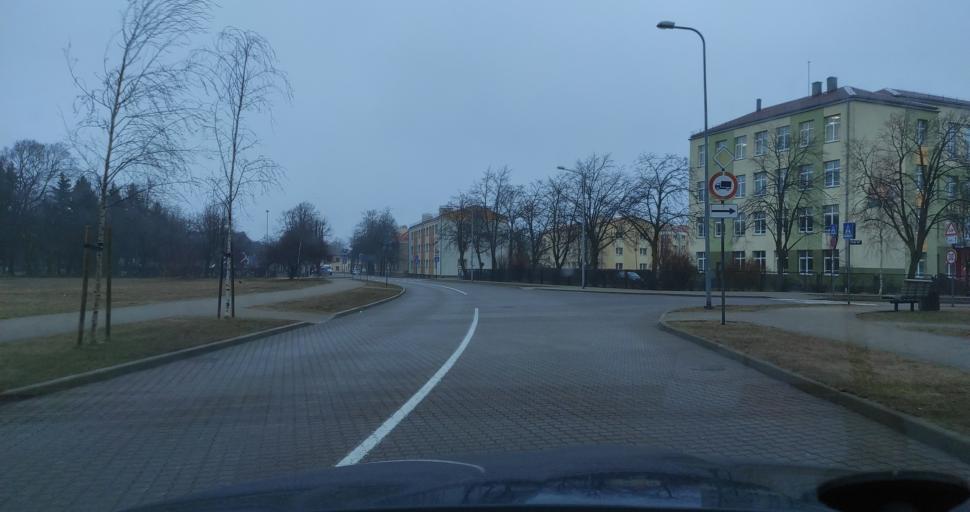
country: LV
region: Ventspils
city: Ventspils
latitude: 57.3872
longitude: 21.5489
